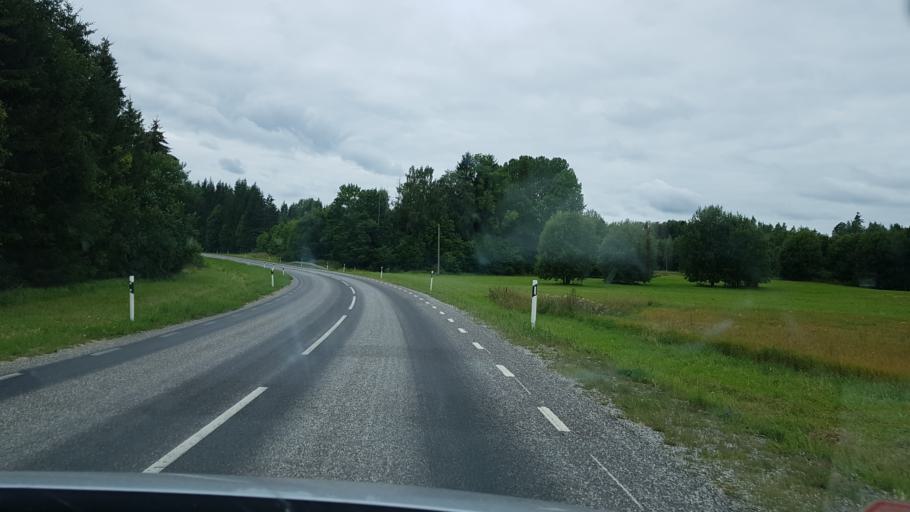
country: EE
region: Vorumaa
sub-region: Antsla vald
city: Vana-Antsla
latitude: 58.0080
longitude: 26.6540
